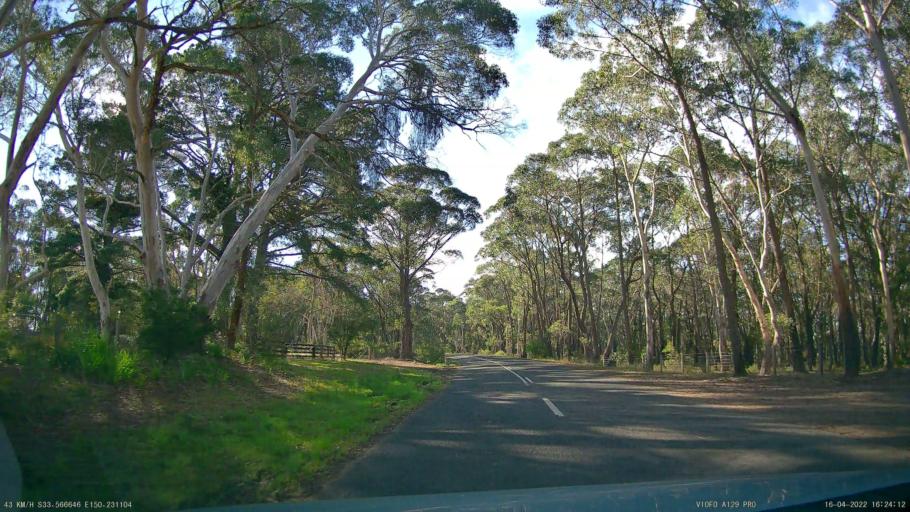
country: AU
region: New South Wales
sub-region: Blue Mountains Municipality
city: Blackheath
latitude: -33.5666
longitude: 150.2311
